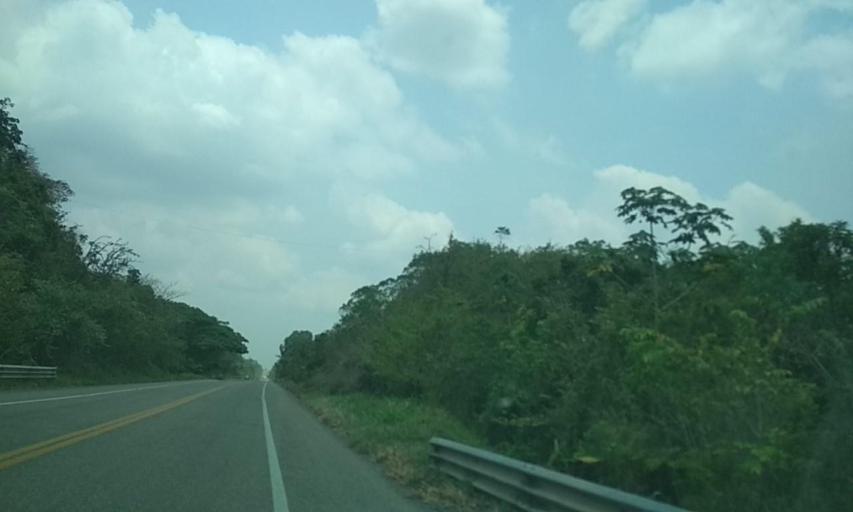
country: MX
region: Tabasco
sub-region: Huimanguillo
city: Francisco Rueda
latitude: 17.6497
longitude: -93.8359
